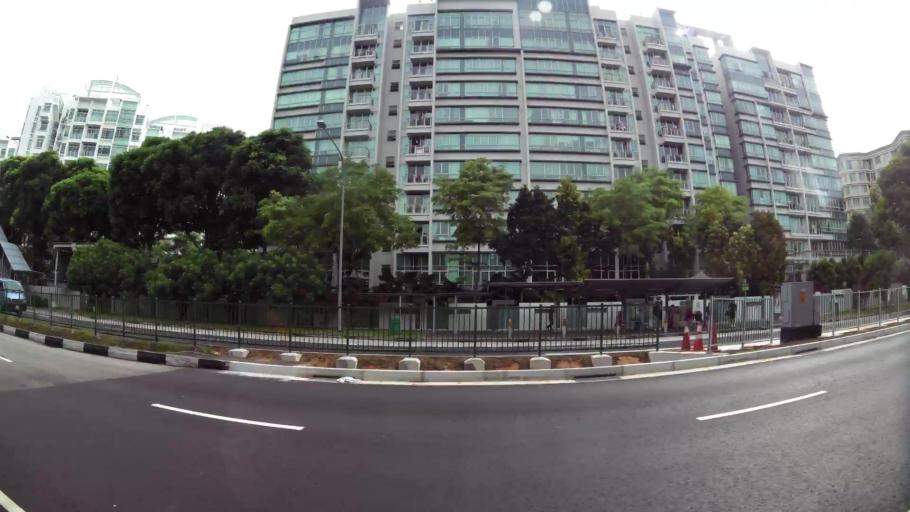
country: SG
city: Singapore
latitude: 1.3346
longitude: 103.7870
